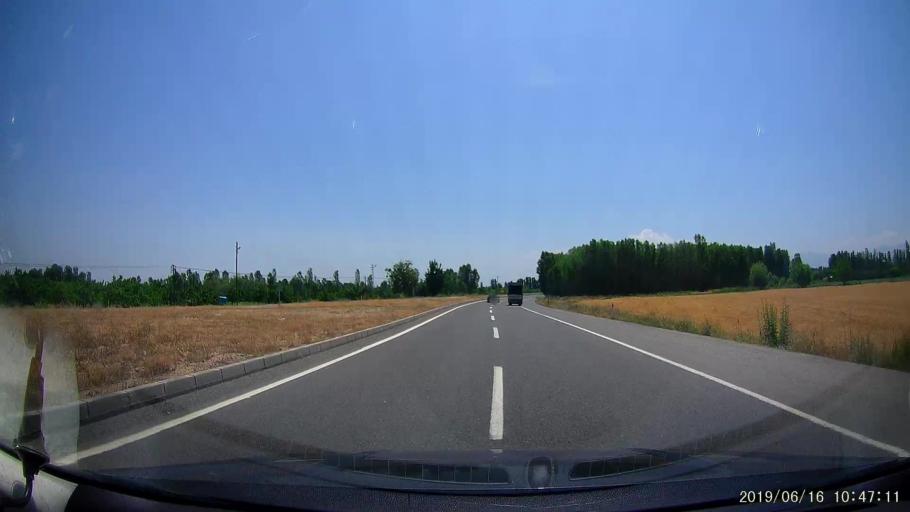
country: AM
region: Armavir
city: Shenavan
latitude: 40.0141
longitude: 43.8864
